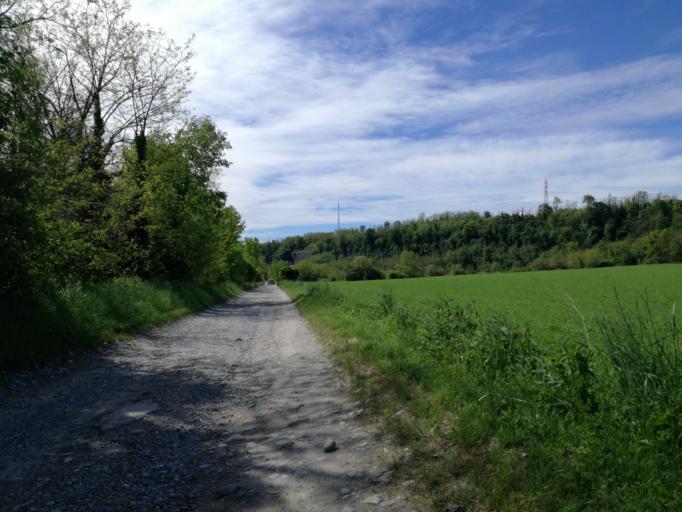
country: IT
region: Lombardy
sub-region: Provincia di Monza e Brianza
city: Porto d'Adda
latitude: 45.6601
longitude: 9.4835
